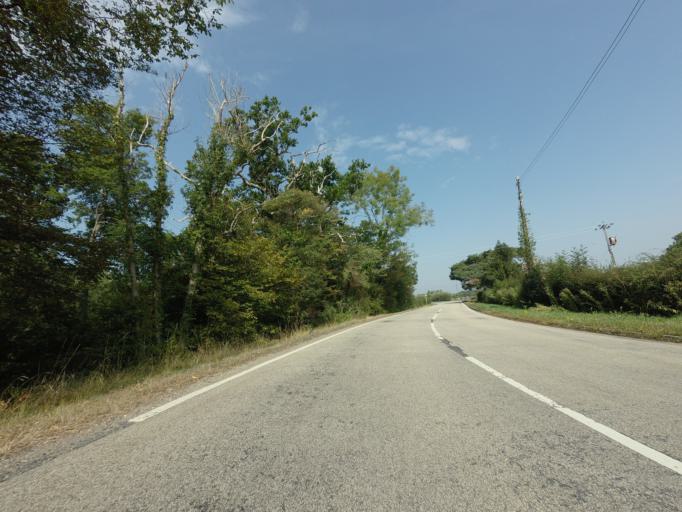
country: GB
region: England
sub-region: Kent
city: Headcorn
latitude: 51.1173
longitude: 0.6106
